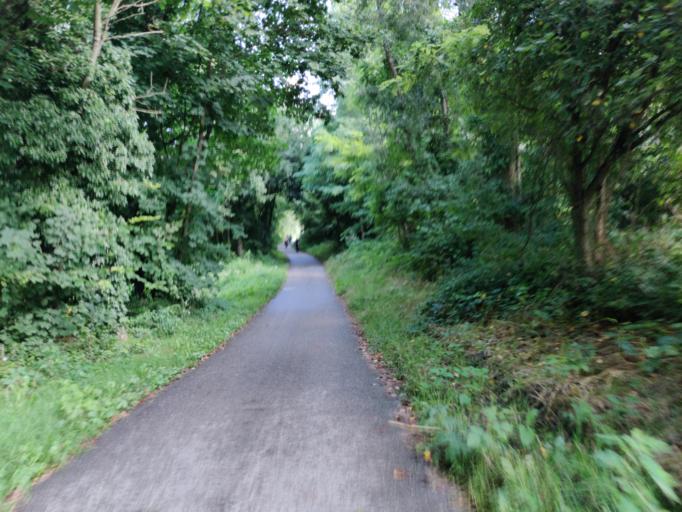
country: AT
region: Lower Austria
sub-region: Politischer Bezirk Krems
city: Aggsbach
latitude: 48.2822
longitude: 15.4020
